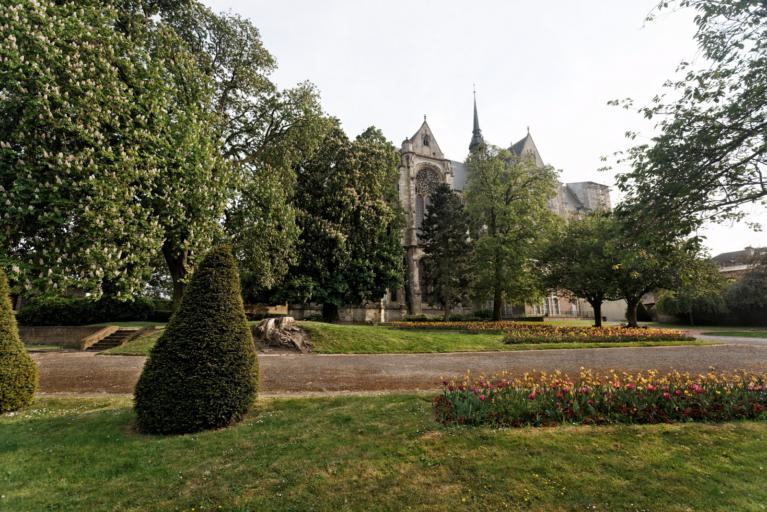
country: FR
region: Picardie
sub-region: Departement de l'Aisne
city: Saint-Quentin
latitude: 49.8487
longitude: 3.2905
